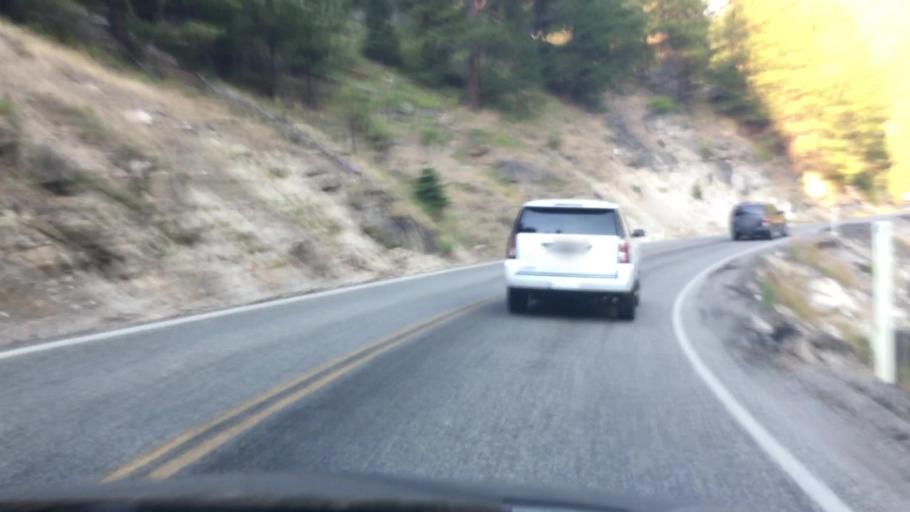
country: US
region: Idaho
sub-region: Valley County
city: Cascade
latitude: 44.3178
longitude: -116.0670
